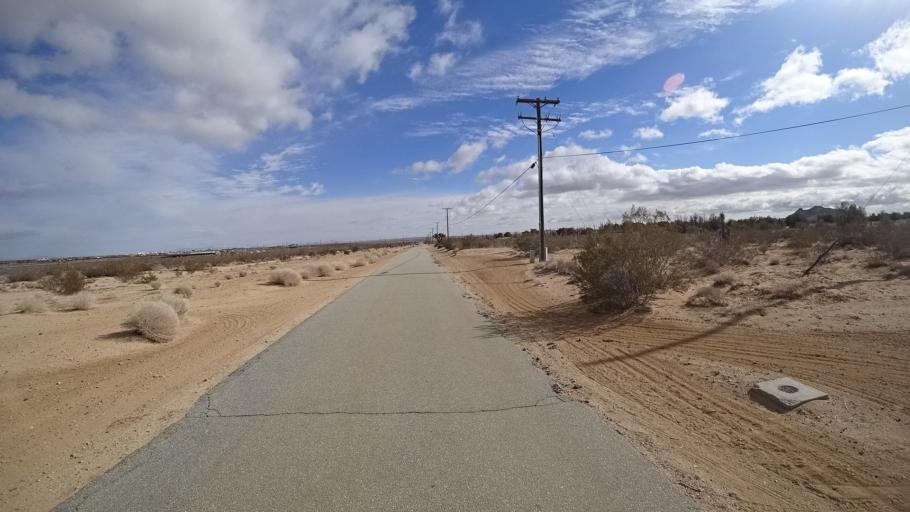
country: US
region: California
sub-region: Kern County
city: Mojave
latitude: 35.0316
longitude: -118.1945
